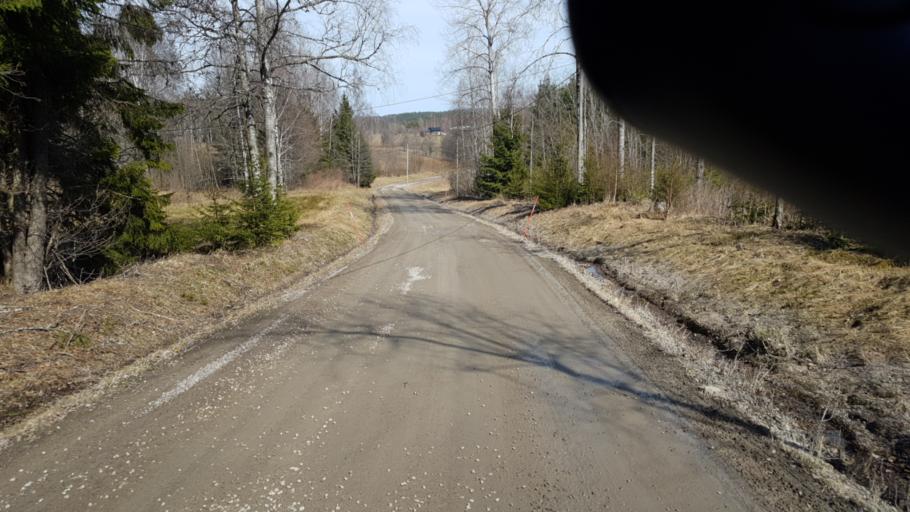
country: SE
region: Vaermland
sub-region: Arvika Kommun
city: Arvika
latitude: 59.5334
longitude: 12.8507
